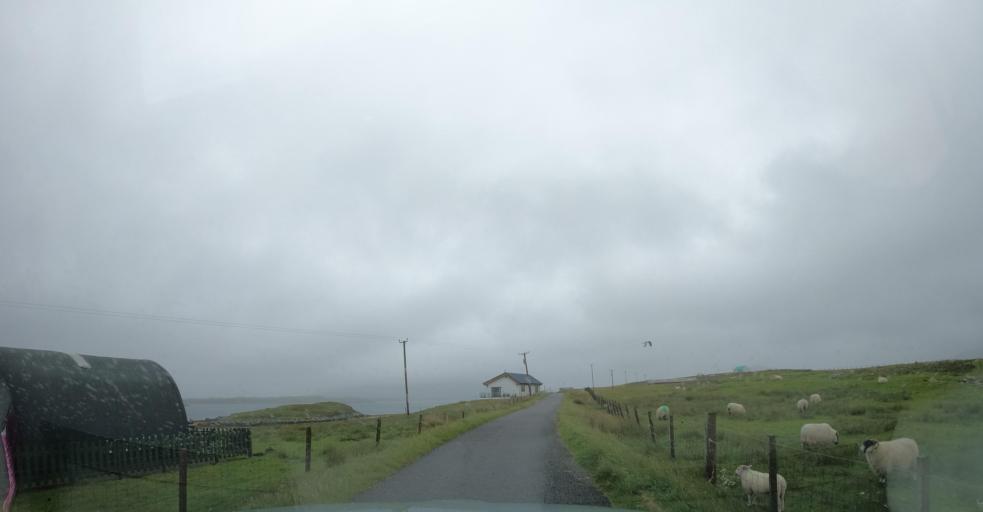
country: GB
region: Scotland
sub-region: Eilean Siar
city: Isle of North Uist
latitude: 57.5516
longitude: -7.2140
